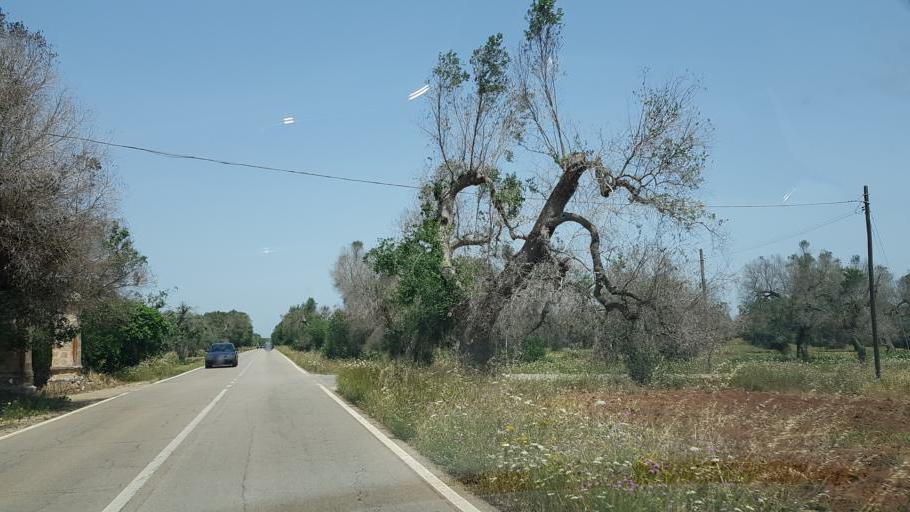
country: IT
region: Apulia
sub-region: Provincia di Lecce
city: Veglie
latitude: 40.3139
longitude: 17.9215
